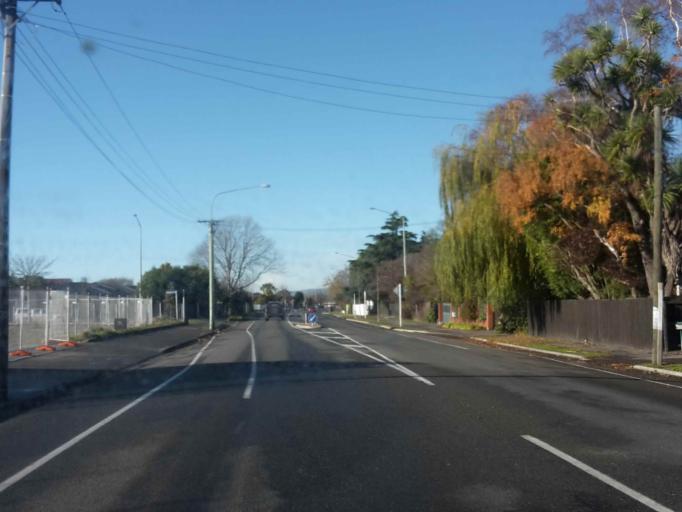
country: NZ
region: Canterbury
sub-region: Christchurch City
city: Christchurch
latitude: -43.5007
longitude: 172.5885
